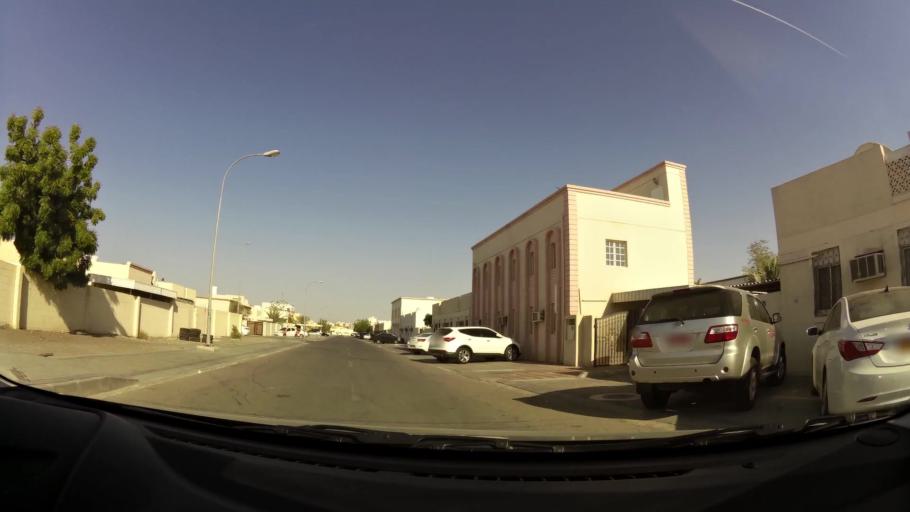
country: OM
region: Muhafazat Masqat
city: As Sib al Jadidah
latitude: 23.6222
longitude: 58.1917
